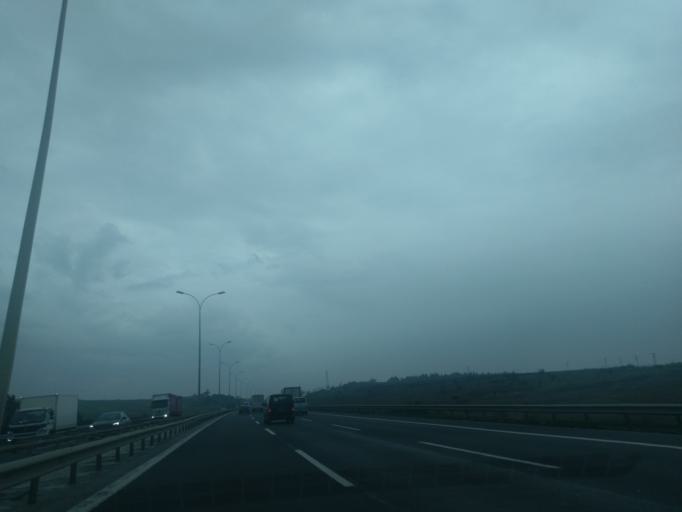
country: TR
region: Istanbul
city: Bueyuekcekmece
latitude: 41.1013
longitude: 28.6065
